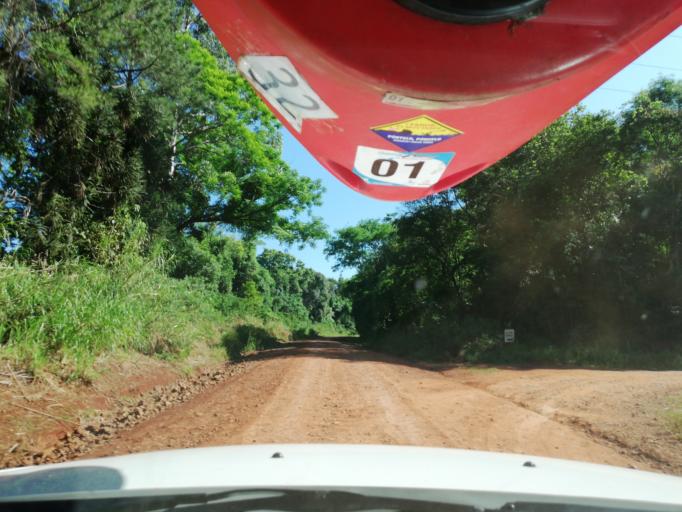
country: AR
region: Misiones
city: Puerto Leoni
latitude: -26.9691
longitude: -55.1646
